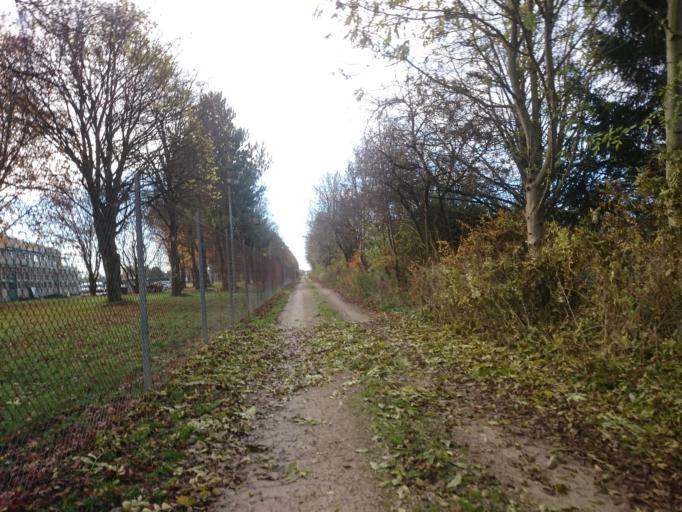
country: DE
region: Bavaria
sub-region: Swabia
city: Konigsbrunn
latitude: 48.2926
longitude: 10.8831
